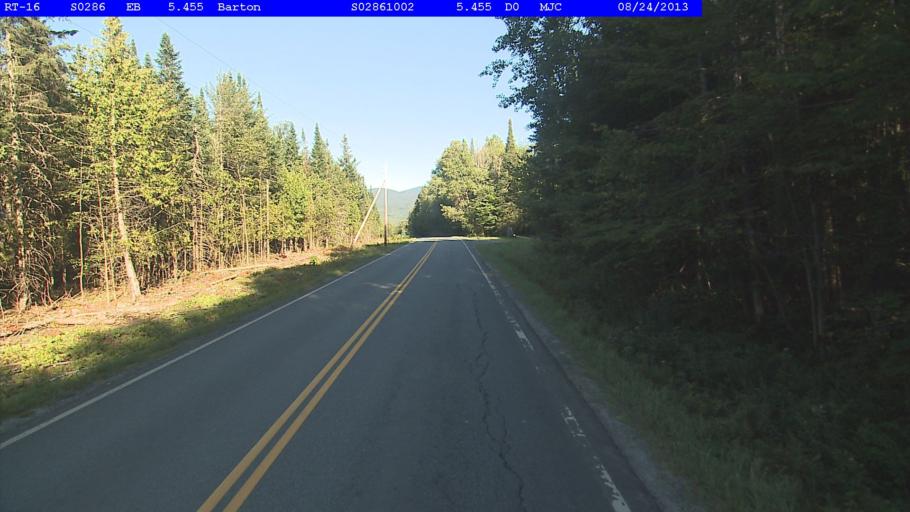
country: US
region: Vermont
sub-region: Orleans County
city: Newport
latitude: 44.7832
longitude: -72.0995
